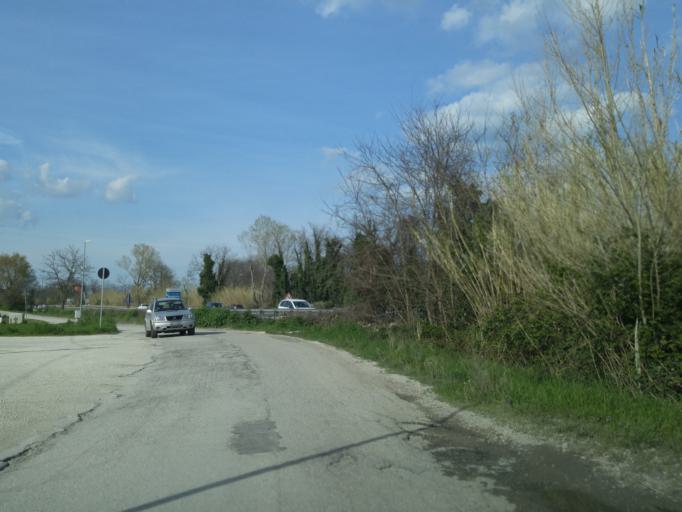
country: IT
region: The Marches
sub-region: Provincia di Pesaro e Urbino
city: Rosciano
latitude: 43.8156
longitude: 13.0170
